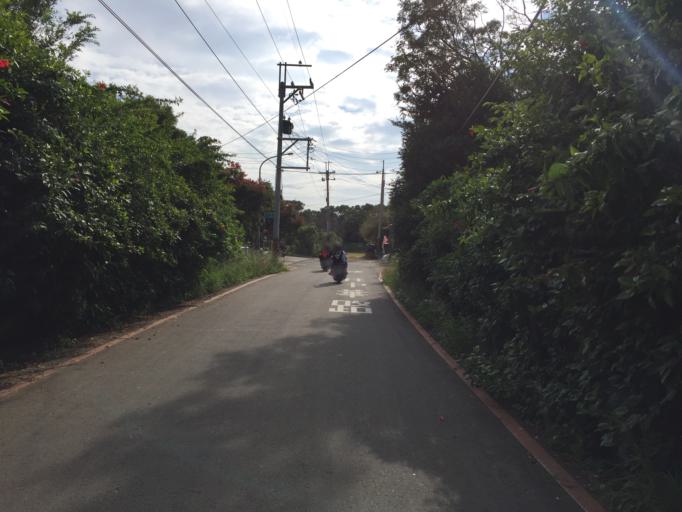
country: TW
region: Taiwan
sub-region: Hsinchu
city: Hsinchu
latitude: 24.7751
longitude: 120.9255
